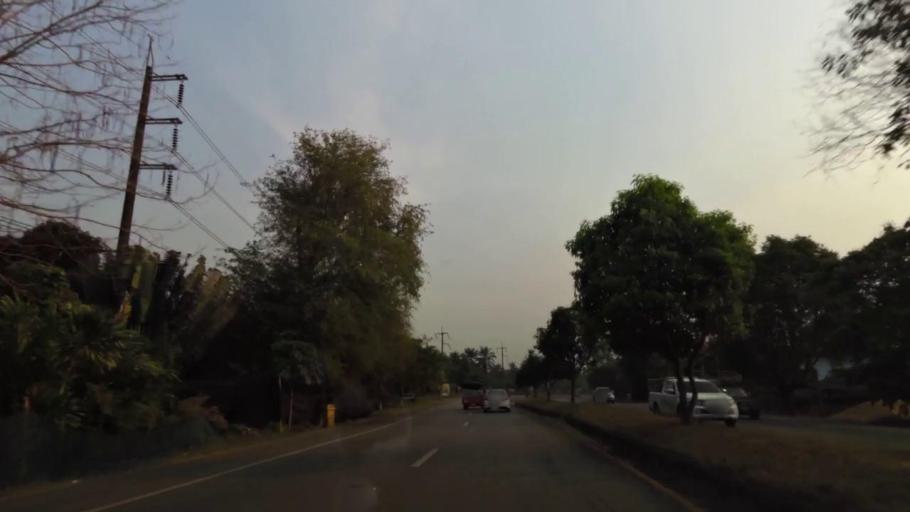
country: TH
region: Chanthaburi
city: Khlung
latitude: 12.5139
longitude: 102.1684
